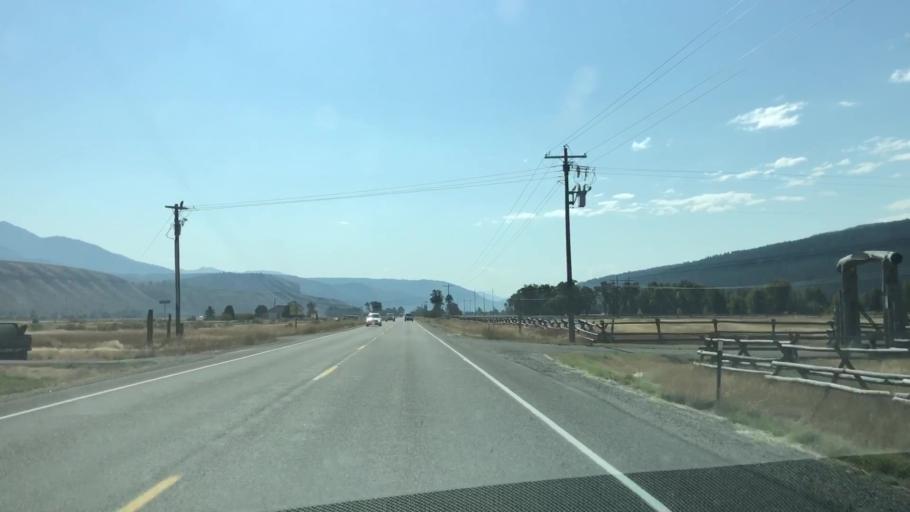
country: US
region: Idaho
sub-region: Teton County
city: Victor
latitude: 43.3969
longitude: -111.2806
